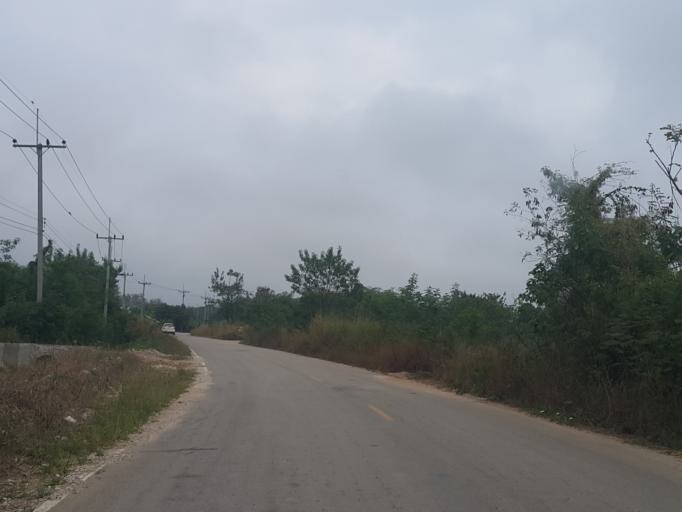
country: TH
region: Lampang
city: Lampang
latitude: 18.3293
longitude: 99.4869
